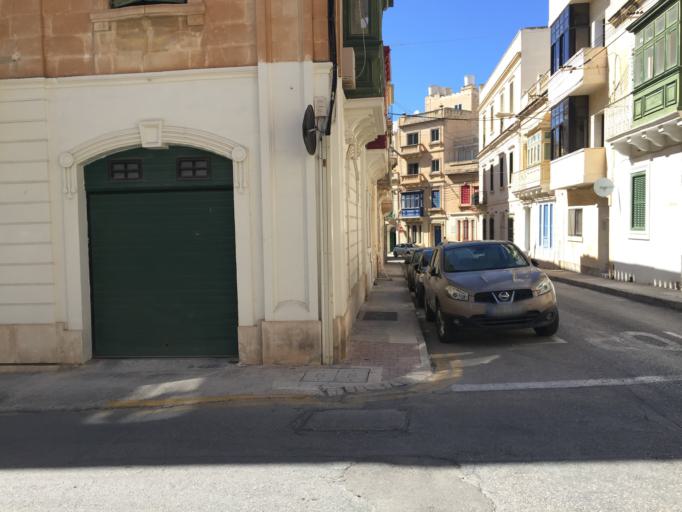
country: MT
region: Tas-Sliema
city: Sliema
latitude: 35.9144
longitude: 14.4997
